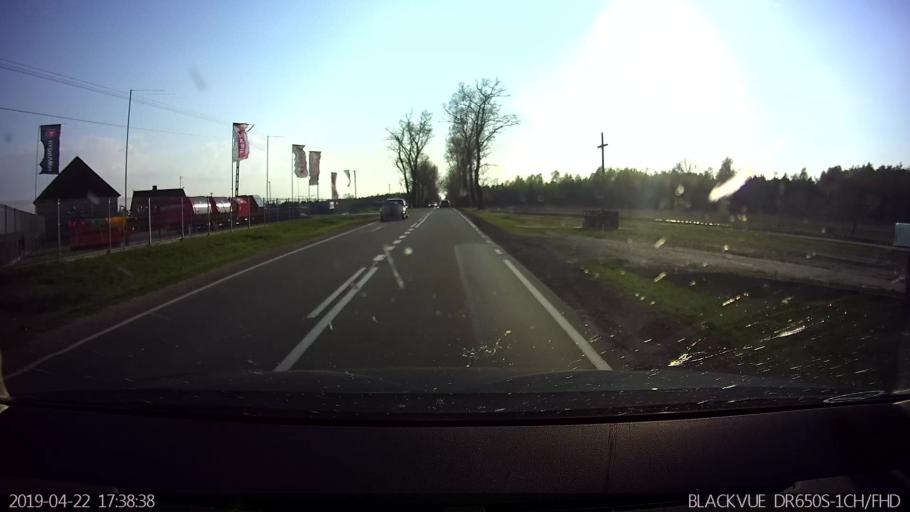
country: PL
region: Masovian Voivodeship
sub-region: Powiat wegrowski
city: Miedzna
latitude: 52.4076
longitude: 22.1575
